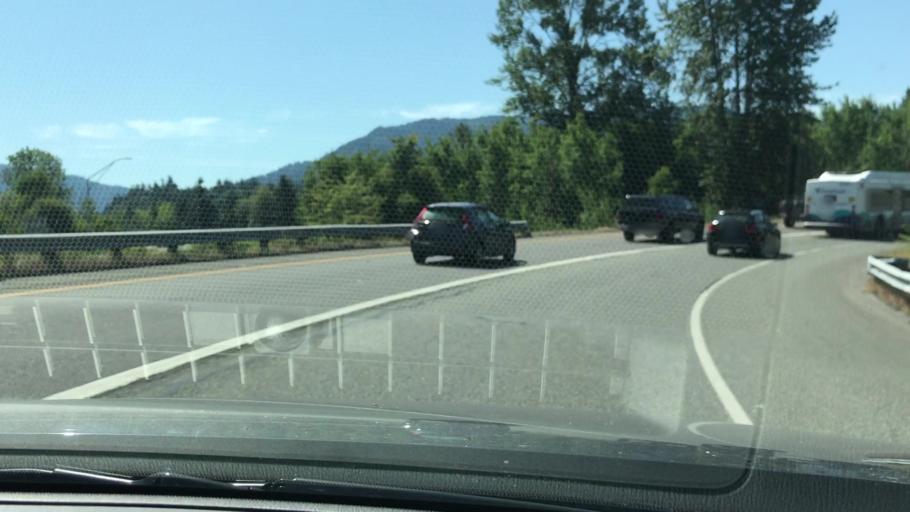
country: US
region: Washington
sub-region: King County
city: Issaquah
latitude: 47.5490
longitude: -122.0585
